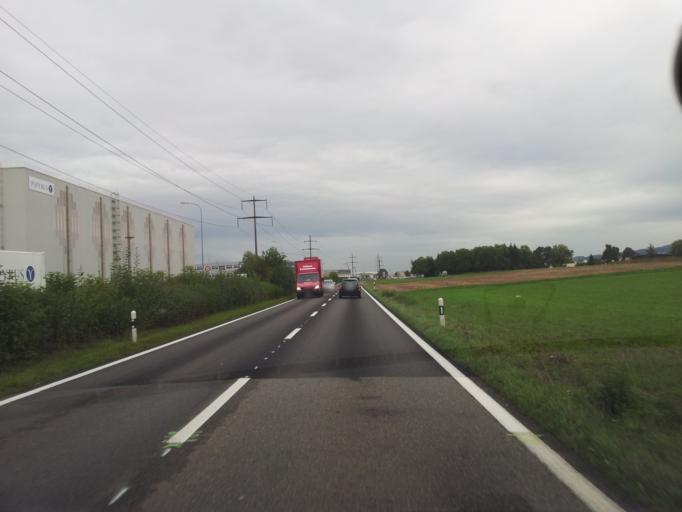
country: CH
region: Aargau
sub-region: Bezirk Bremgarten
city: Dottikon
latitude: 47.3748
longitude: 8.2246
